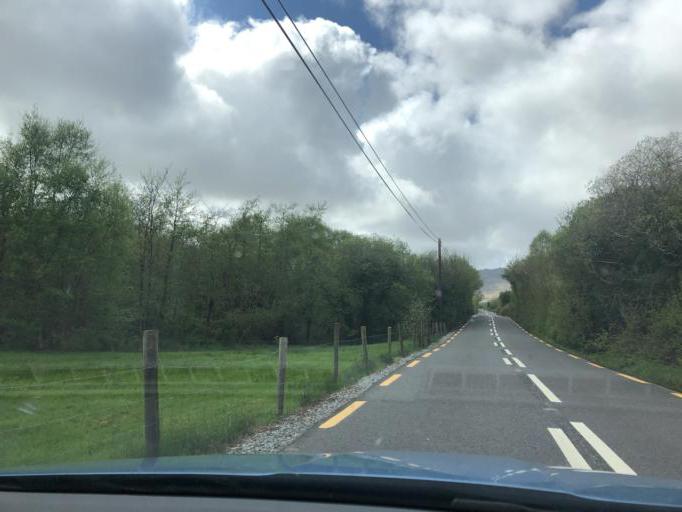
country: IE
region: Munster
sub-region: Ciarrai
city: Cahersiveen
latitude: 51.8295
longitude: -9.9377
